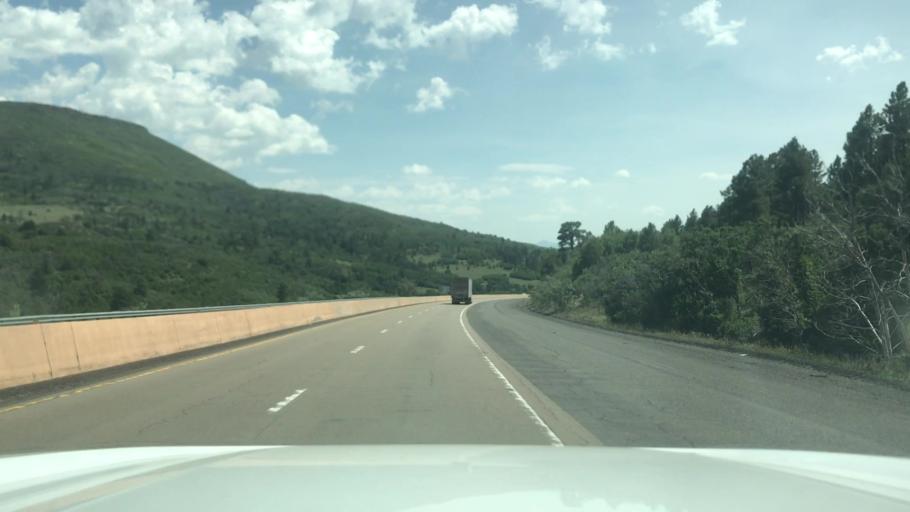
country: US
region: New Mexico
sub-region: Colfax County
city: Raton
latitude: 36.9757
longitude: -104.4796
